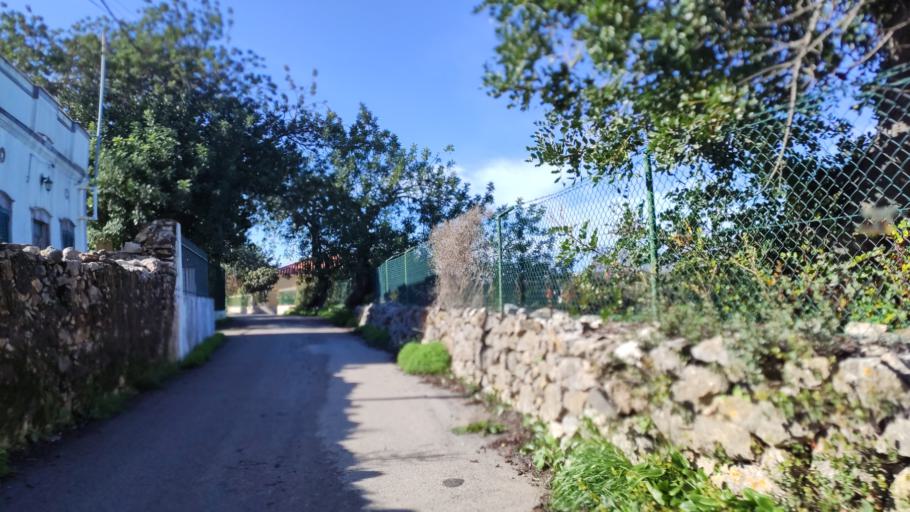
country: PT
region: Faro
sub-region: Sao Bras de Alportel
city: Sao Bras de Alportel
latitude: 37.1502
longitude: -7.8723
